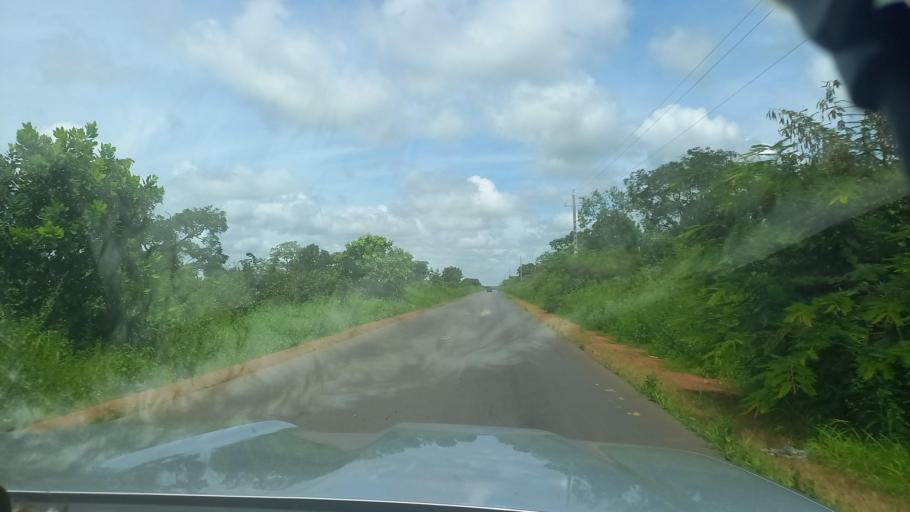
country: GM
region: Lower River
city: Kaiaf
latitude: 13.1876
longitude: -15.5577
